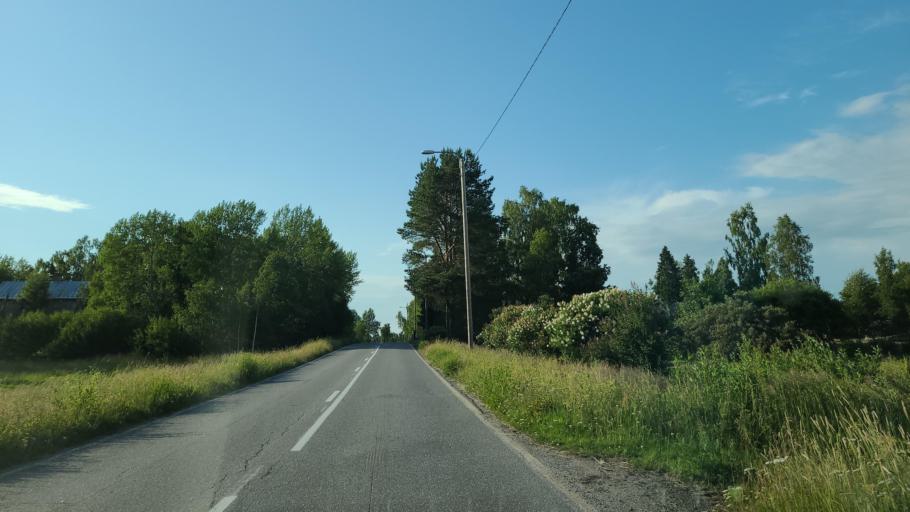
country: FI
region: Ostrobothnia
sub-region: Vaasa
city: Replot
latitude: 63.3348
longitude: 21.3341
